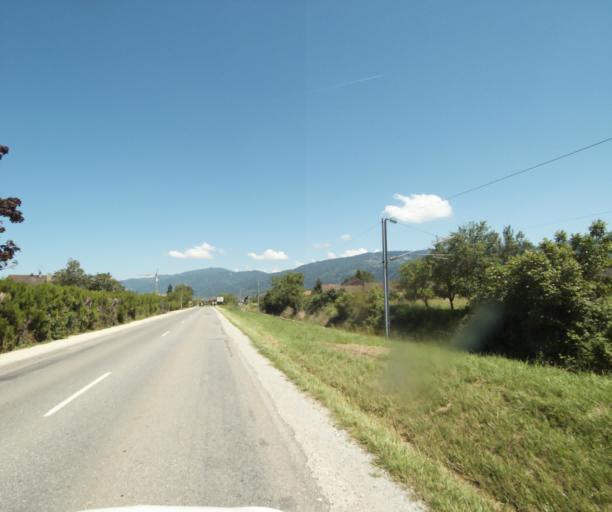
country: FR
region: Rhone-Alpes
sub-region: Departement de la Haute-Savoie
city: Bons-en-Chablais
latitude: 46.2716
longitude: 6.3574
